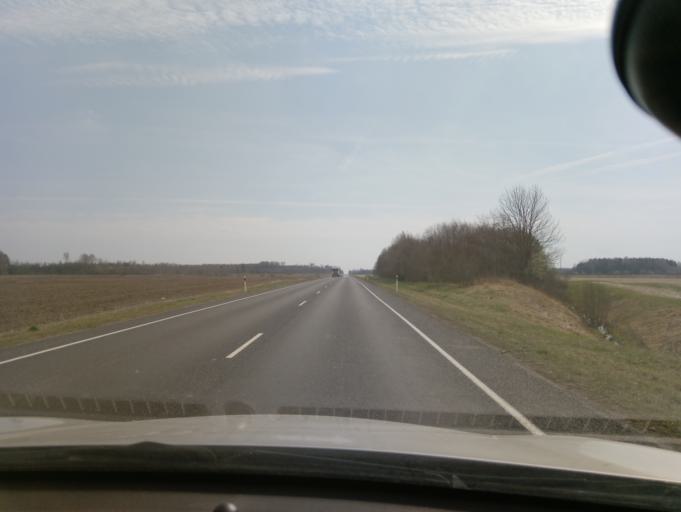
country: EE
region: Viljandimaa
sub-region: Vohma linn
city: Vohma
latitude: 58.7358
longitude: 25.5886
